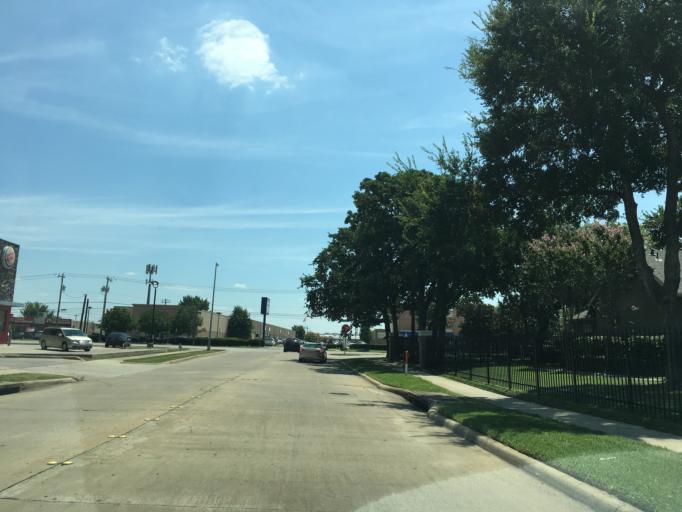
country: US
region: Texas
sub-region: Denton County
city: Lewisville
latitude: 33.0245
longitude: -96.9939
